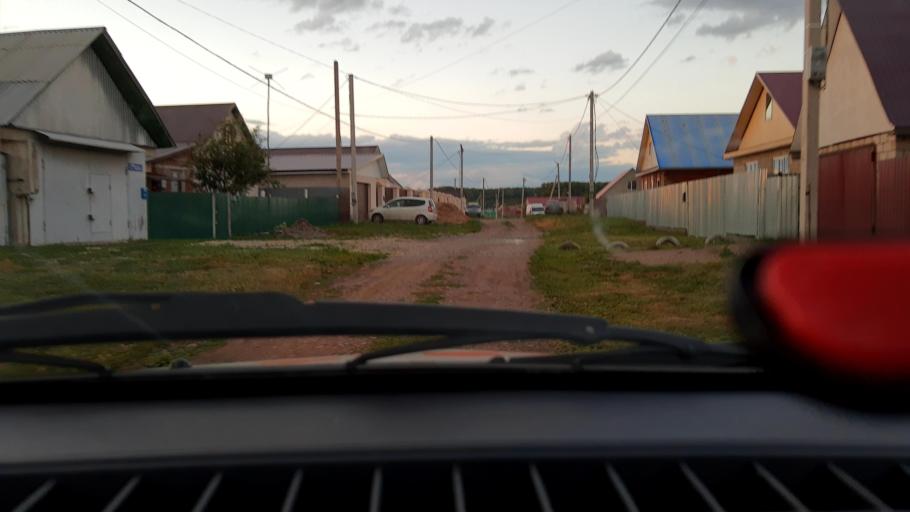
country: RU
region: Bashkortostan
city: Kabakovo
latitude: 54.5147
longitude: 55.9472
